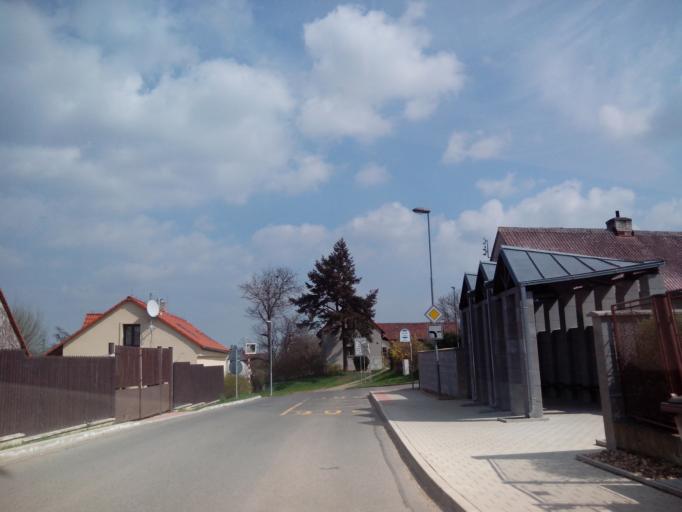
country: CZ
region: Central Bohemia
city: Zdice
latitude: 49.8836
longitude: 13.9566
